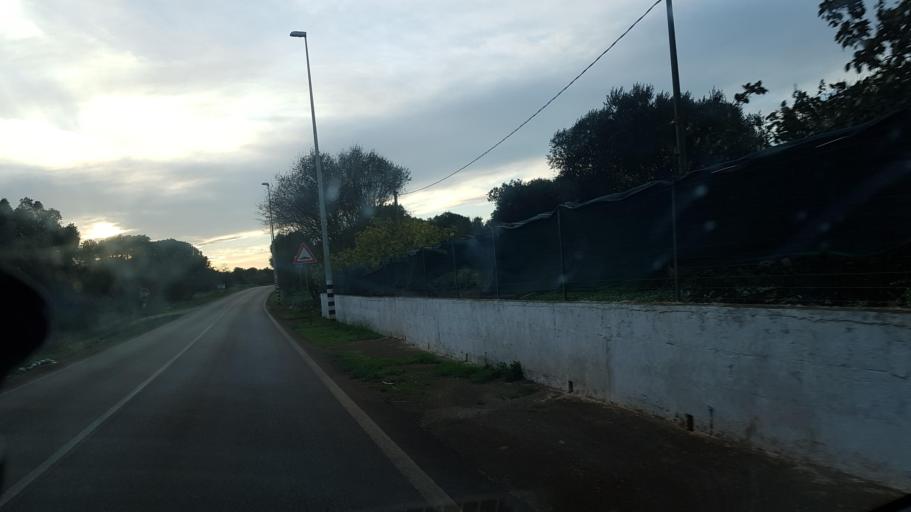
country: IT
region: Apulia
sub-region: Provincia di Brindisi
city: San Michele Salentino
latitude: 40.6457
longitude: 17.6606
